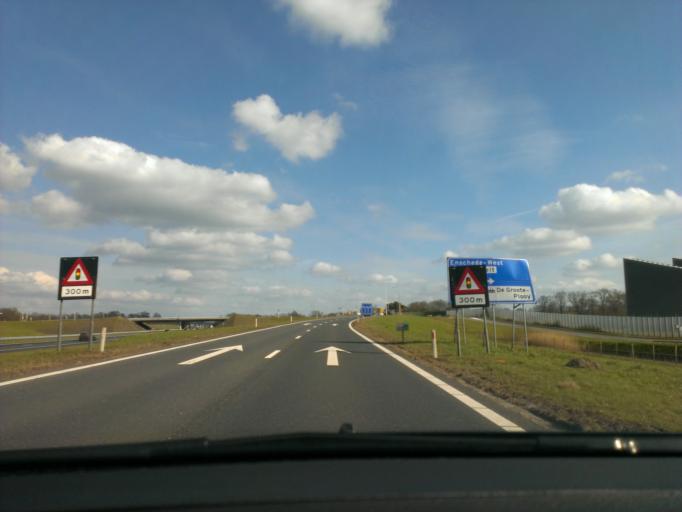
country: NL
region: Overijssel
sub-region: Gemeente Hengelo
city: Hengelo
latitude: 52.2079
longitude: 6.8189
